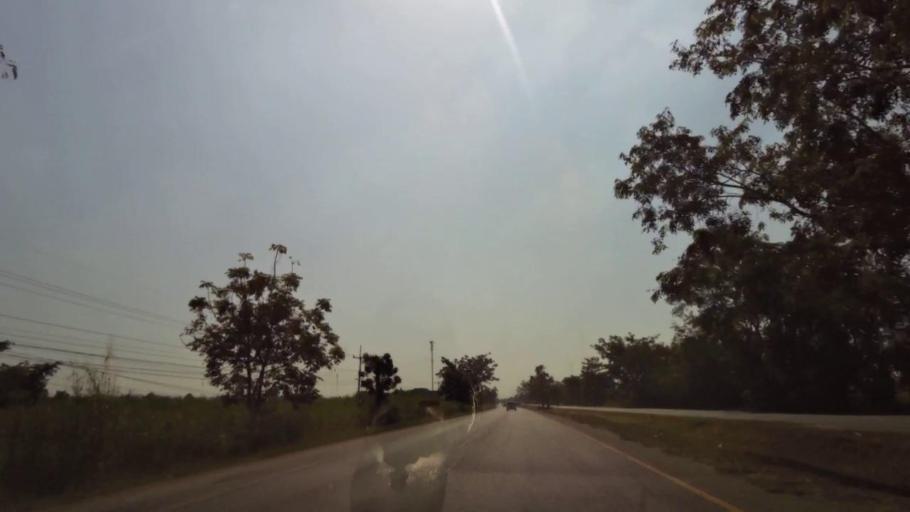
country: TH
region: Phichit
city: Wachira Barami
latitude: 16.3619
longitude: 100.1303
